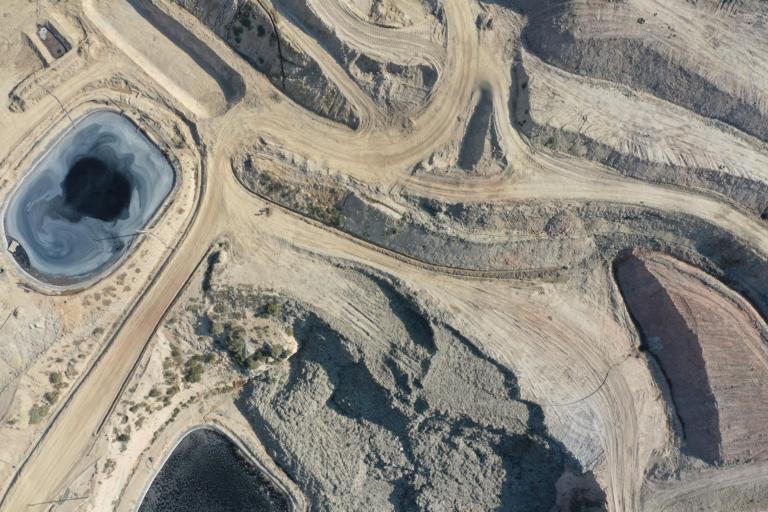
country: BO
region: La Paz
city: La Paz
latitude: -16.5584
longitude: -68.1271
